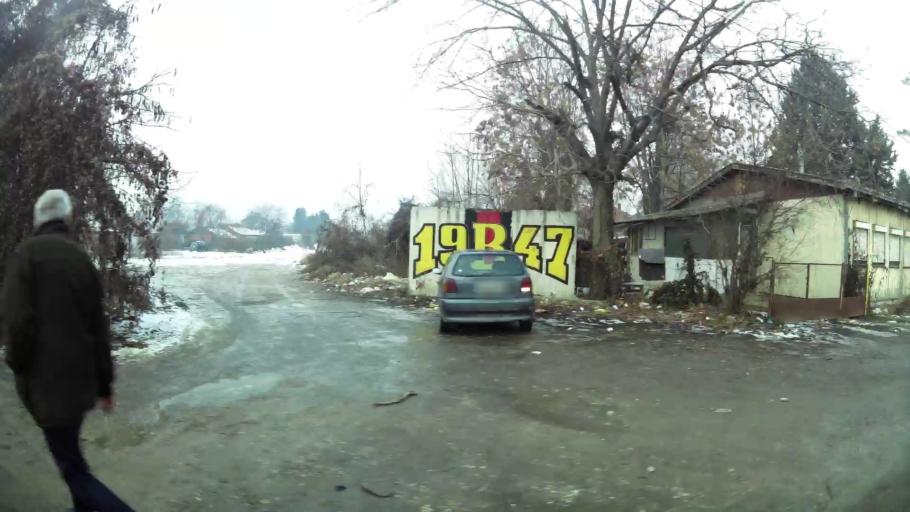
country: MK
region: Kisela Voda
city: Kisela Voda
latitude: 41.9953
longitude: 21.5004
